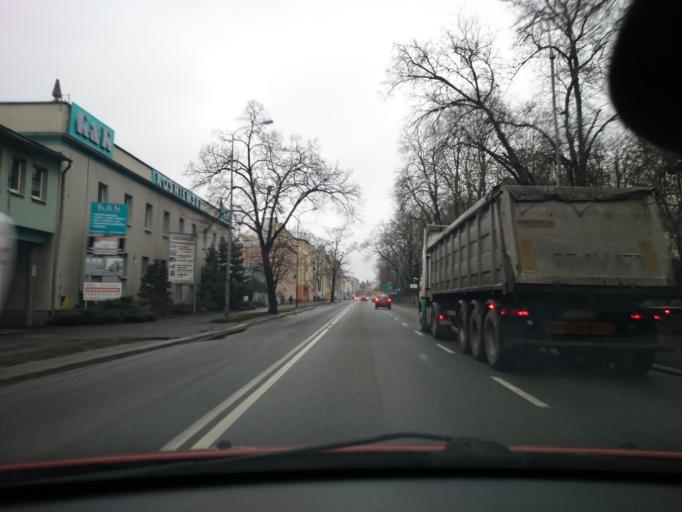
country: PL
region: Opole Voivodeship
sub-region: Powiat opolski
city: Opole
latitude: 50.6737
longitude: 17.9095
